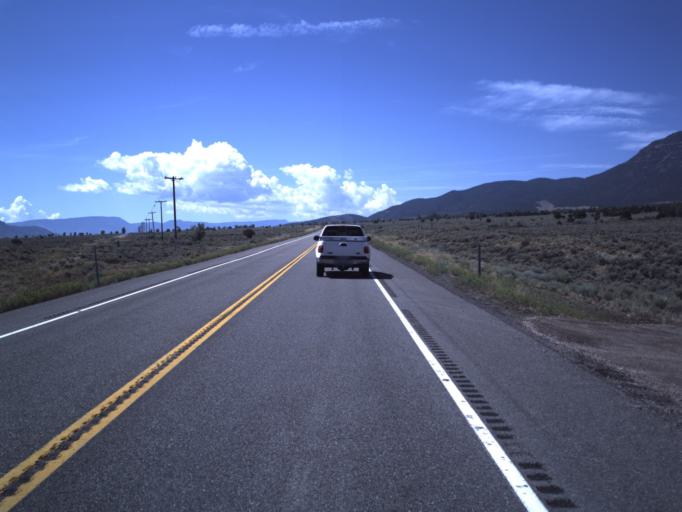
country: US
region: Utah
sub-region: Piute County
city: Junction
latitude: 38.4013
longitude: -112.2312
